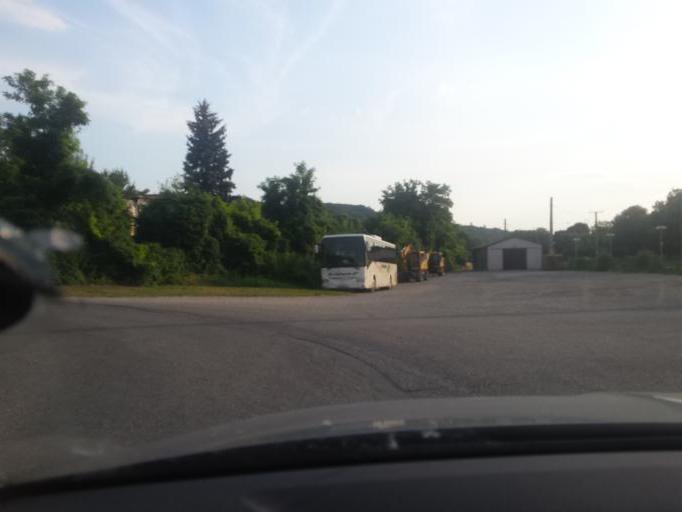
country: AT
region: Lower Austria
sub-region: Politischer Bezirk Bruck an der Leitha
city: Hainburg an der Donau
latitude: 48.1449
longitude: 16.9326
